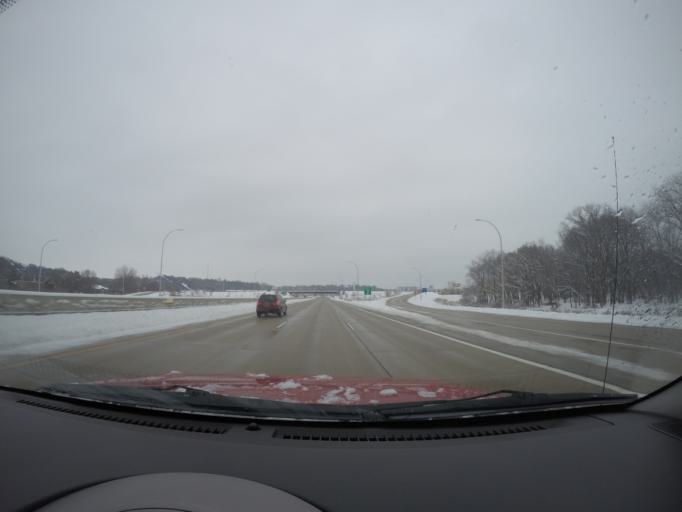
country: US
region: Minnesota
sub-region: Olmsted County
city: Rochester
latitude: 43.9983
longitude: -92.4845
